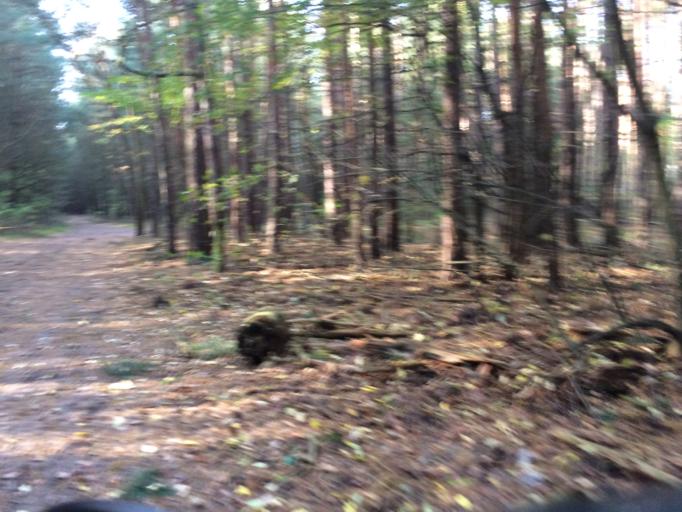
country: DE
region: Brandenburg
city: Glienicke
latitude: 52.6723
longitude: 13.3547
